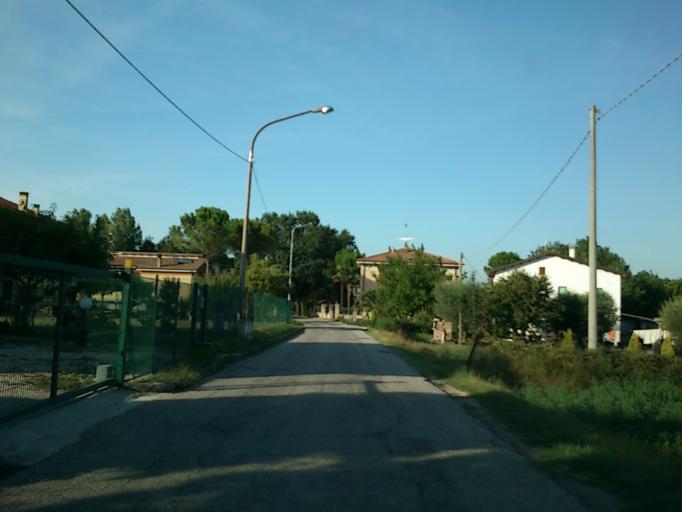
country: IT
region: The Marches
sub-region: Provincia di Pesaro e Urbino
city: Saltara
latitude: 43.7404
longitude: 12.9088
